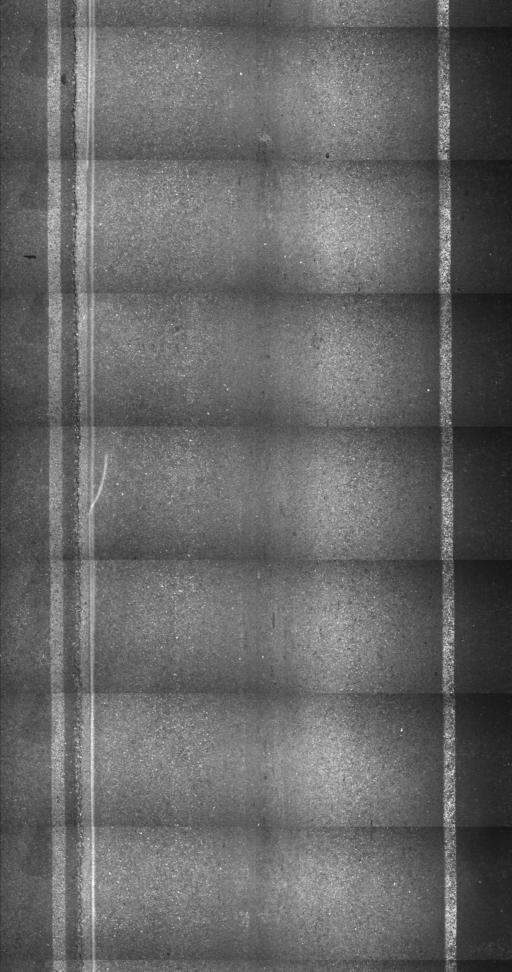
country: CA
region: Quebec
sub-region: Monteregie
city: Sutton
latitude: 44.9820
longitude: -72.5108
